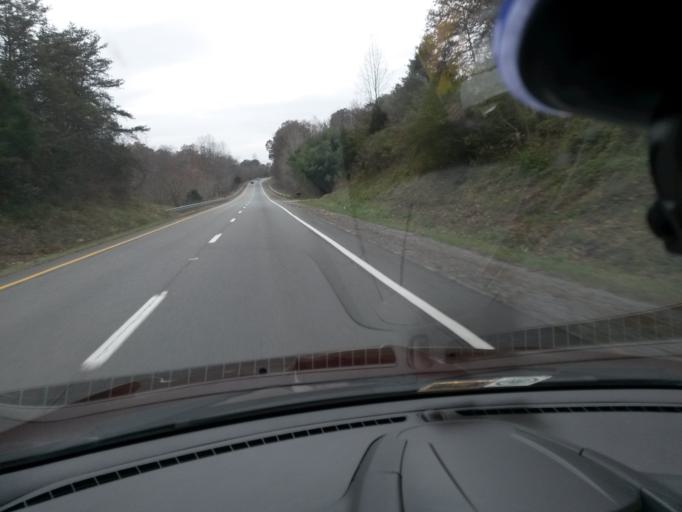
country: US
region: Virginia
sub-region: Nelson County
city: Nellysford
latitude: 37.8433
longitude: -78.7800
